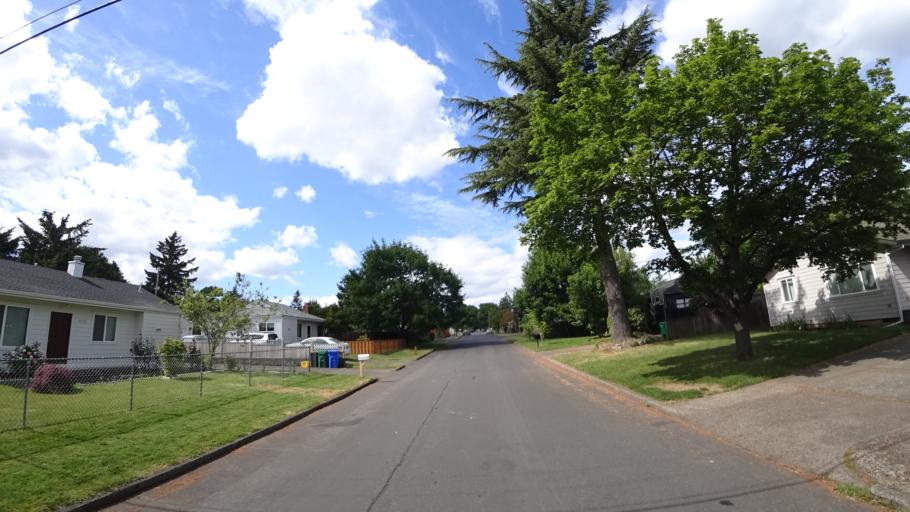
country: US
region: Oregon
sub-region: Multnomah County
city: Lents
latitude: 45.4909
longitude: -122.5457
